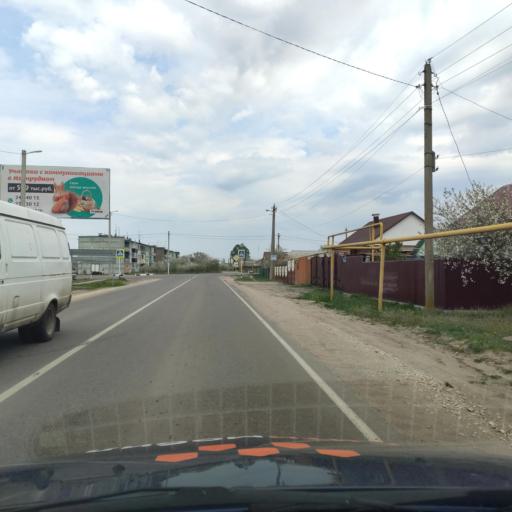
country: RU
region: Voronezj
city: Podgornoye
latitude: 51.8873
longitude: 39.1730
